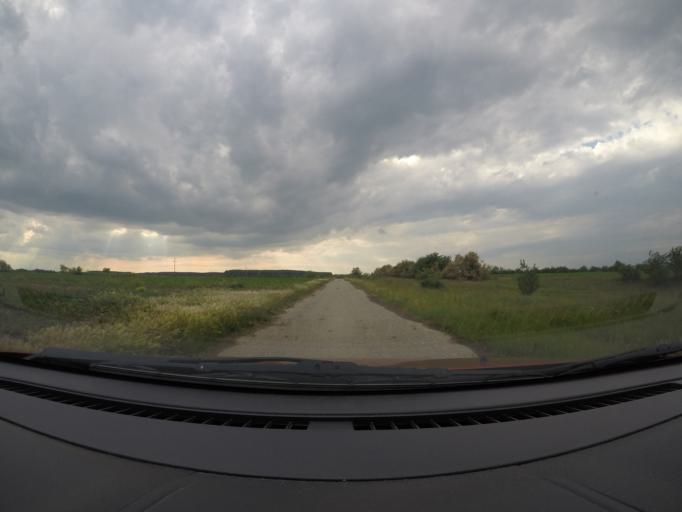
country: RS
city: Uzdin
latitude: 45.2032
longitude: 20.6074
